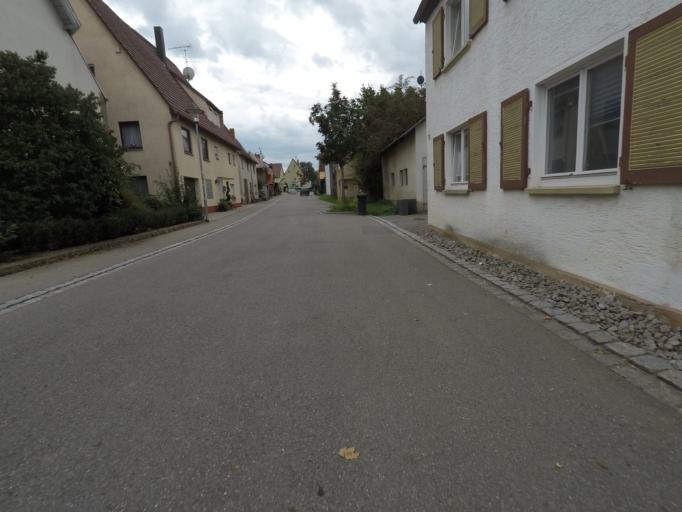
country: DE
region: Baden-Wuerttemberg
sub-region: Regierungsbezirk Stuttgart
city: Herrenberg
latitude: 48.5575
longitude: 8.9016
